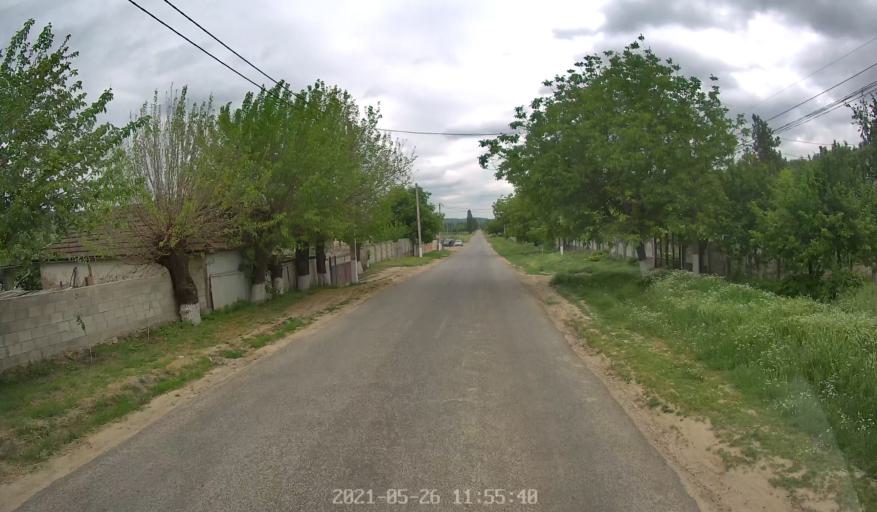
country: MD
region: Hincesti
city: Dancu
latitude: 46.7856
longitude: 28.3498
